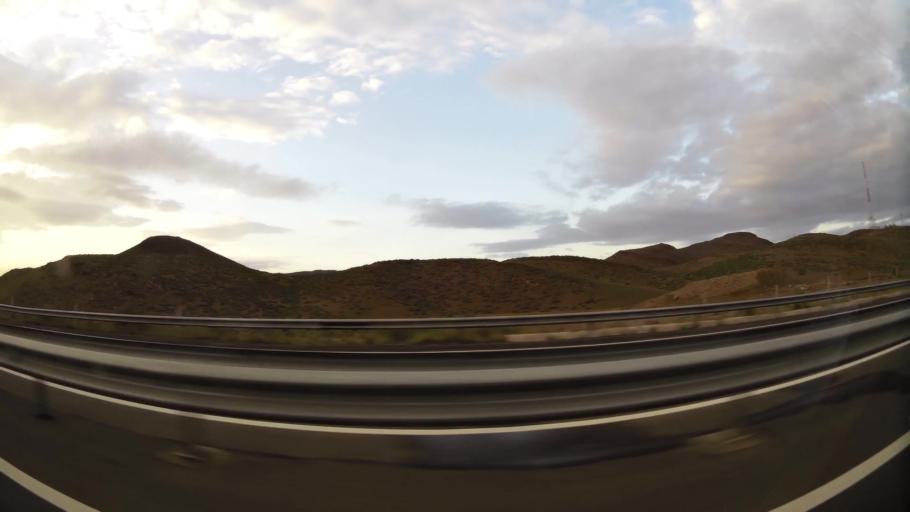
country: MA
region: Oriental
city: Taourirt
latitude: 34.4674
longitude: -3.0211
